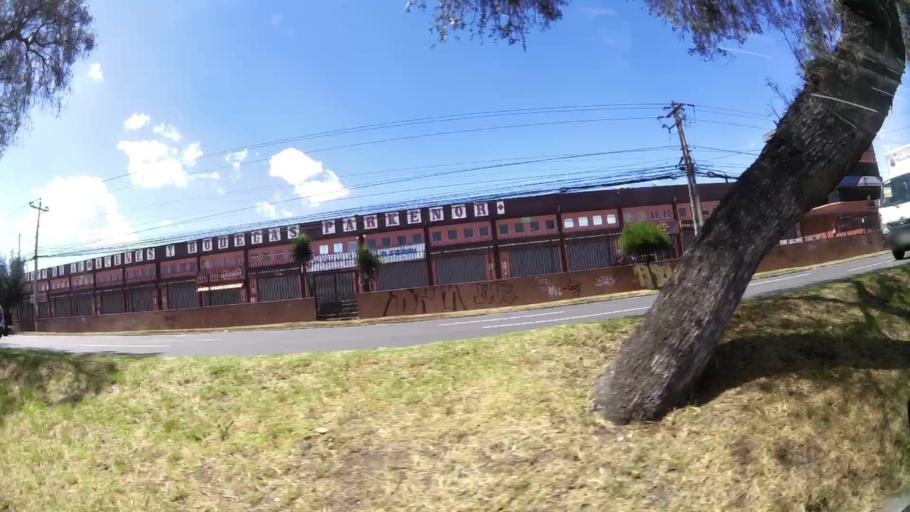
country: EC
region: Pichincha
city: Quito
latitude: -0.1098
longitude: -78.4785
